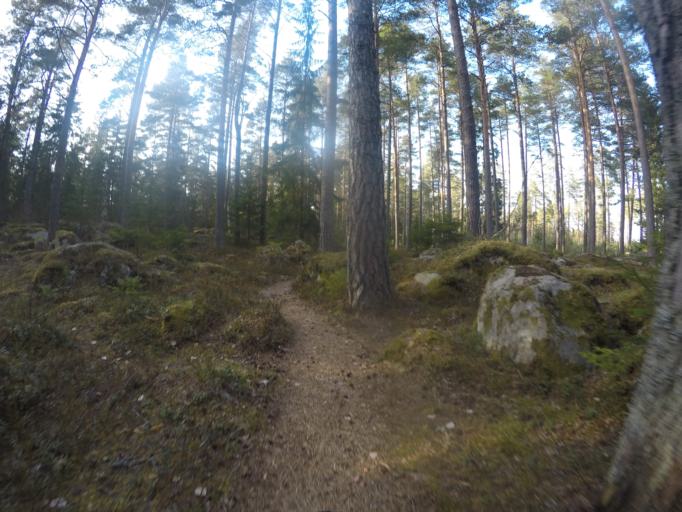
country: SE
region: Soedermanland
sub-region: Eskilstuna Kommun
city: Hallbybrunn
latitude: 59.3944
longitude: 16.4085
